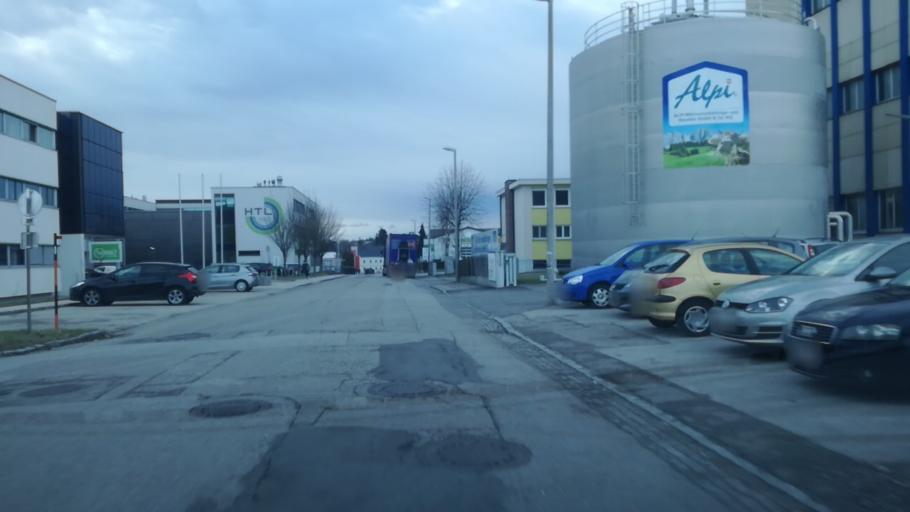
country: AT
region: Upper Austria
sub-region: Politischer Bezirk Ried im Innkreis
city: Ried im Innkreis
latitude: 48.2023
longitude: 13.4847
